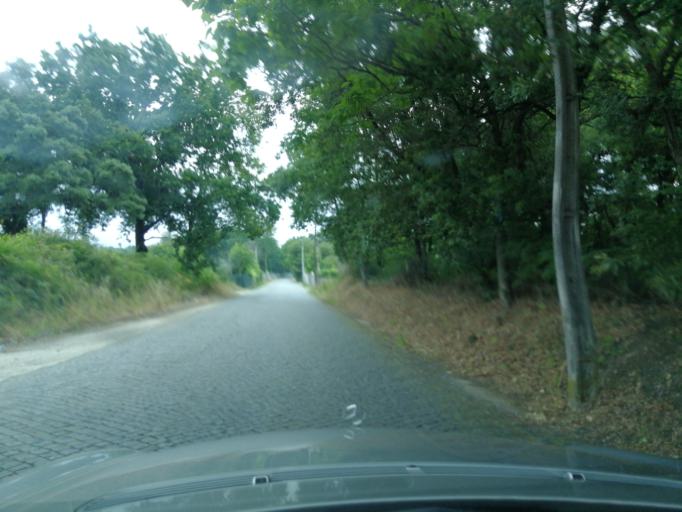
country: PT
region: Braga
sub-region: Vila Verde
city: Prado
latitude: 41.5974
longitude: -8.4534
